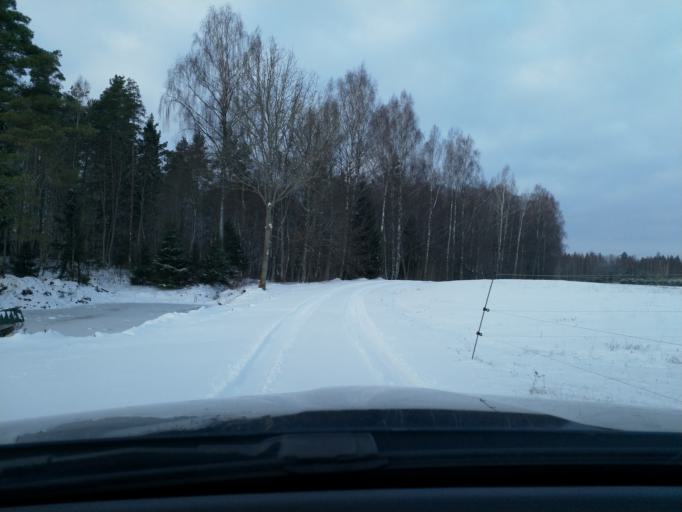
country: LV
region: Kuldigas Rajons
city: Kuldiga
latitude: 56.8639
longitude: 21.8842
